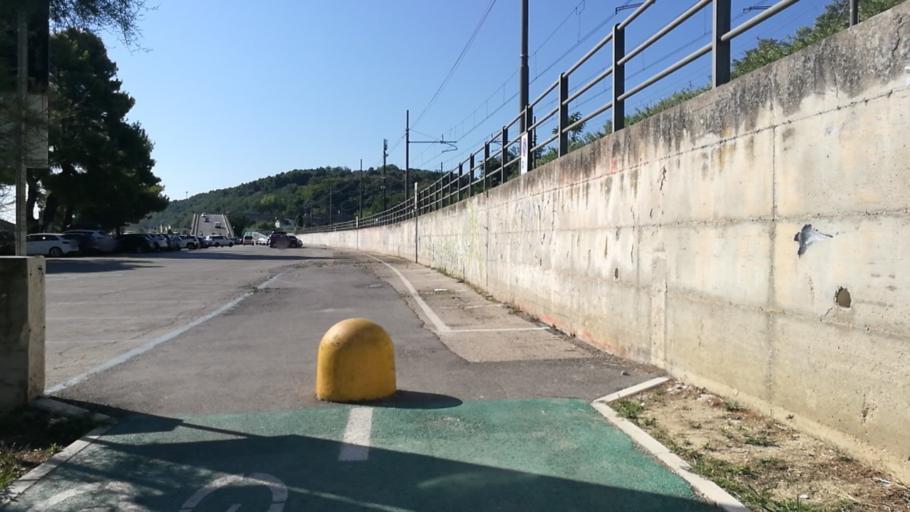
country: IT
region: Abruzzo
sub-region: Provincia di Chieti
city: Ortona
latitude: 42.3475
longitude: 14.4095
